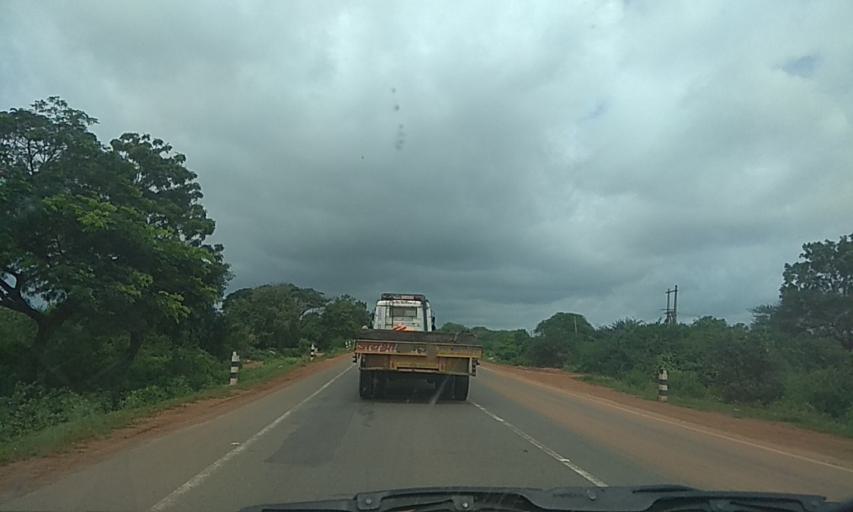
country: IN
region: Karnataka
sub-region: Dharwad
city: Hubli
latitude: 15.3345
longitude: 75.0953
